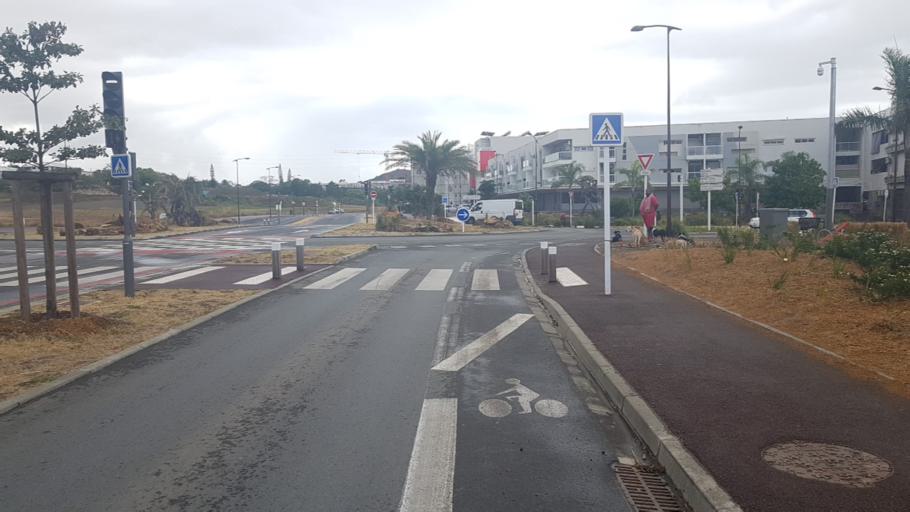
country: NC
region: South Province
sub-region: Noumea
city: Noumea
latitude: -22.2186
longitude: 166.4736
